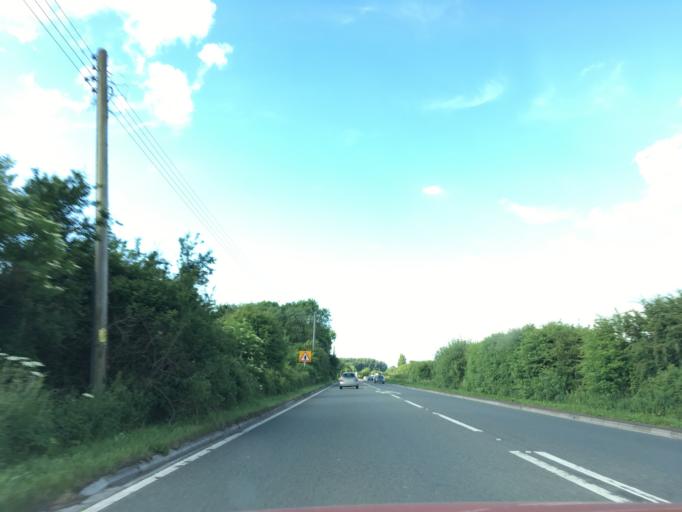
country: GB
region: England
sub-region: Somerset
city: Highbridge
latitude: 51.1951
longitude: -2.9951
